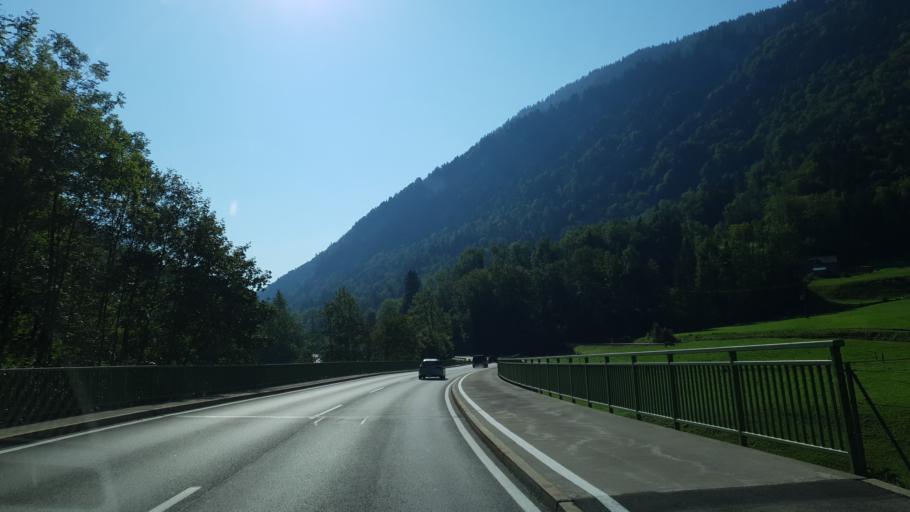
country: AT
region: Vorarlberg
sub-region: Politischer Bezirk Bregenz
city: Reuthe
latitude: 47.3896
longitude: 9.8545
